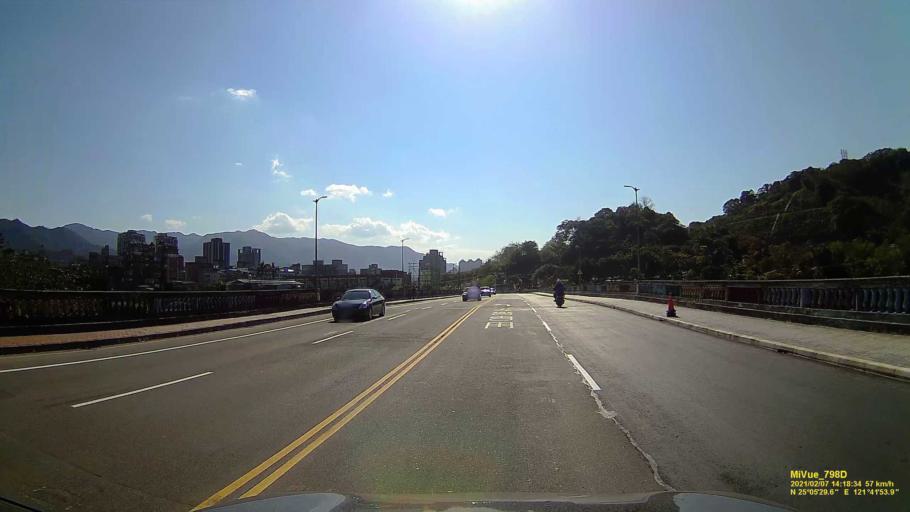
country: TW
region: Taiwan
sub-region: Keelung
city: Keelung
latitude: 25.0914
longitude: 121.6981
